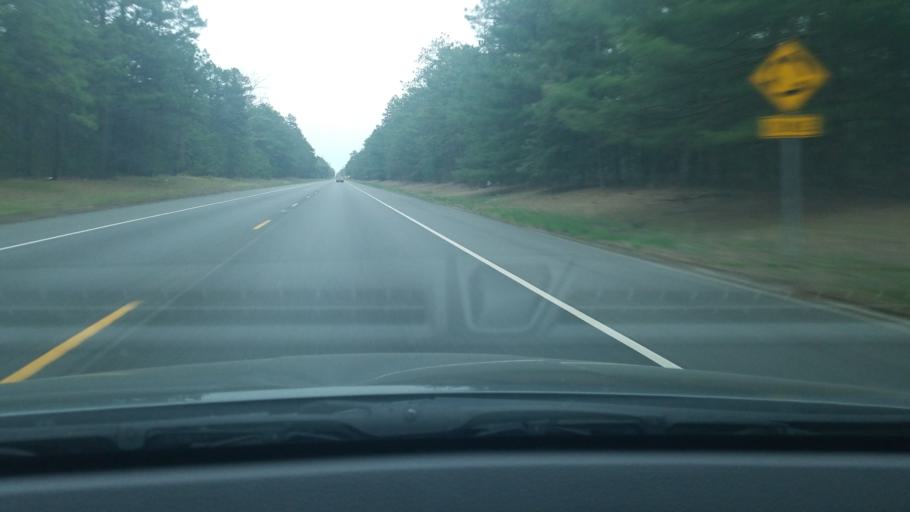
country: US
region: New Jersey
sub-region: Burlington County
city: Presidential Lakes Estates
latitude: 39.8954
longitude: -74.6081
